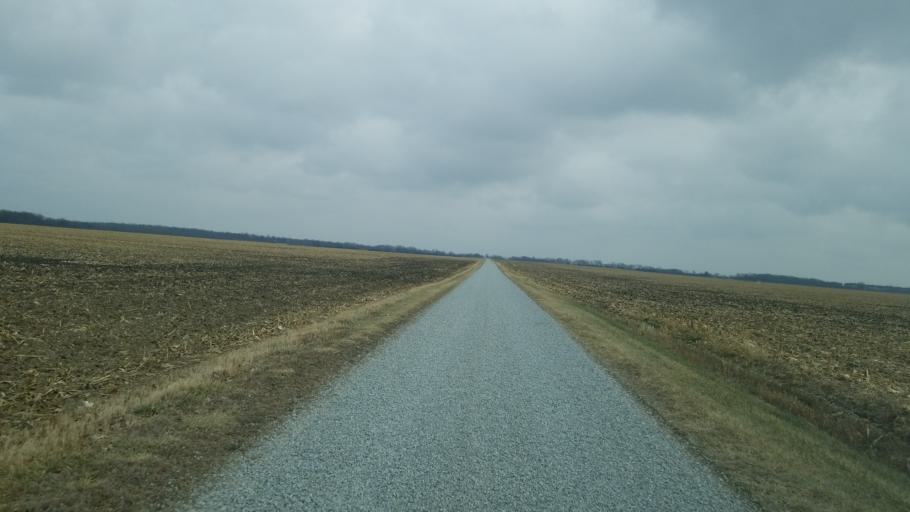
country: US
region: Ohio
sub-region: Wyandot County
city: Upper Sandusky
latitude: 40.7600
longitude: -83.2550
